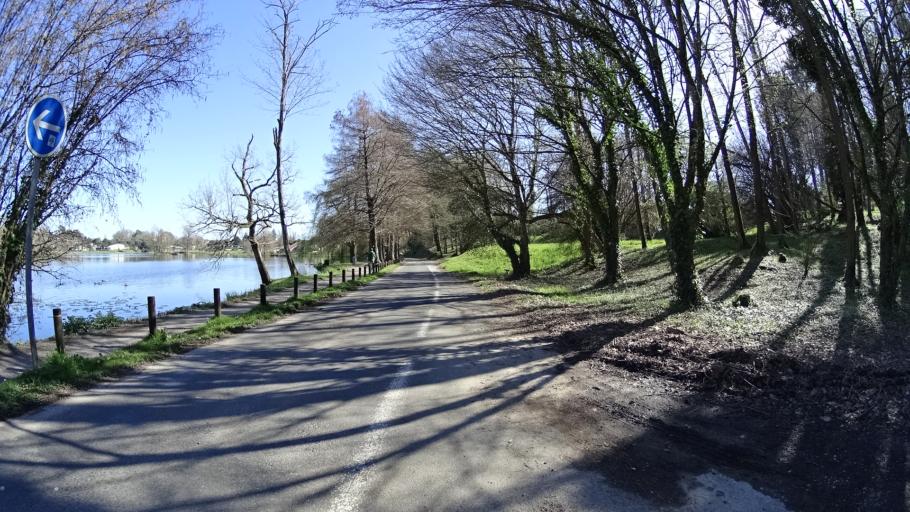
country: FR
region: Aquitaine
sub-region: Departement des Landes
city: Saint-Paul-les-Dax
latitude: 43.7295
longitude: -1.0708
